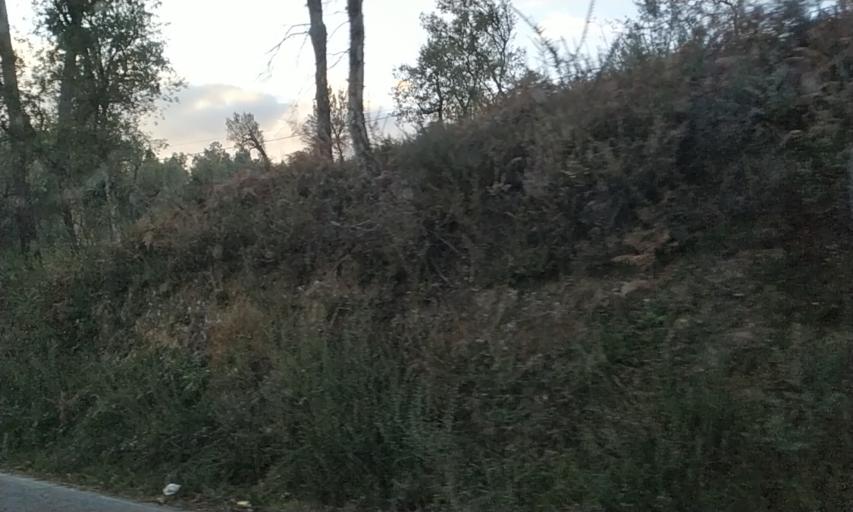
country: PT
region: Vila Real
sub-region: Mondim de Basto
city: Mondim de Basto
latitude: 41.4411
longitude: -7.9714
